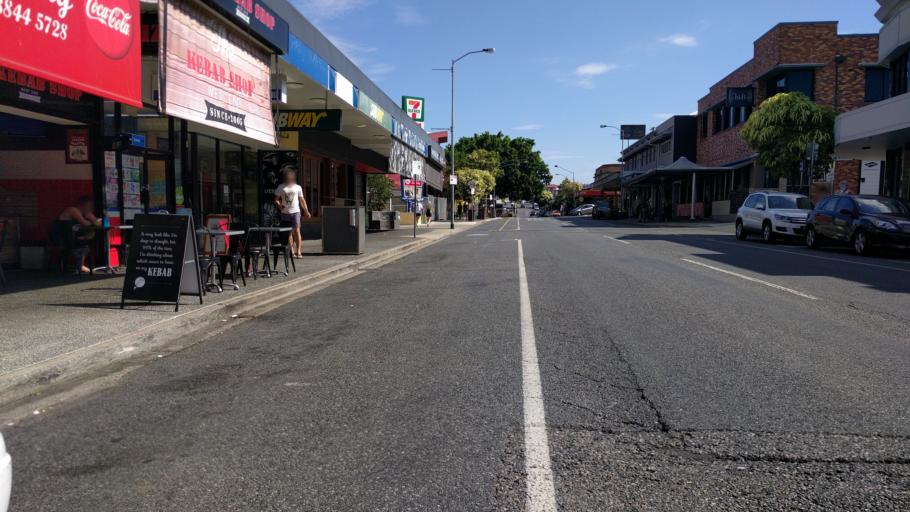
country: AU
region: Queensland
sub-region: Brisbane
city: South Brisbane
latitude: -27.4783
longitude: 153.0126
